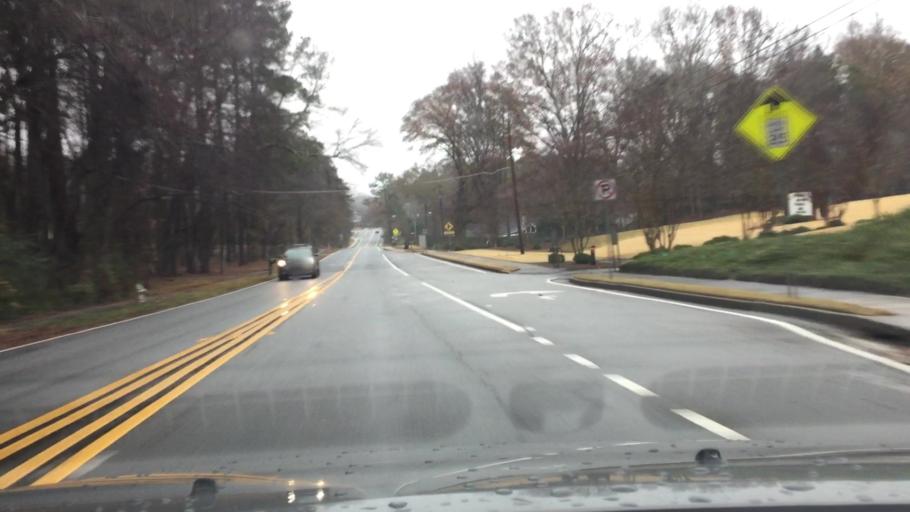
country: US
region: Georgia
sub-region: Cobb County
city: Powder Springs
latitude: 33.8906
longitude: -84.6763
